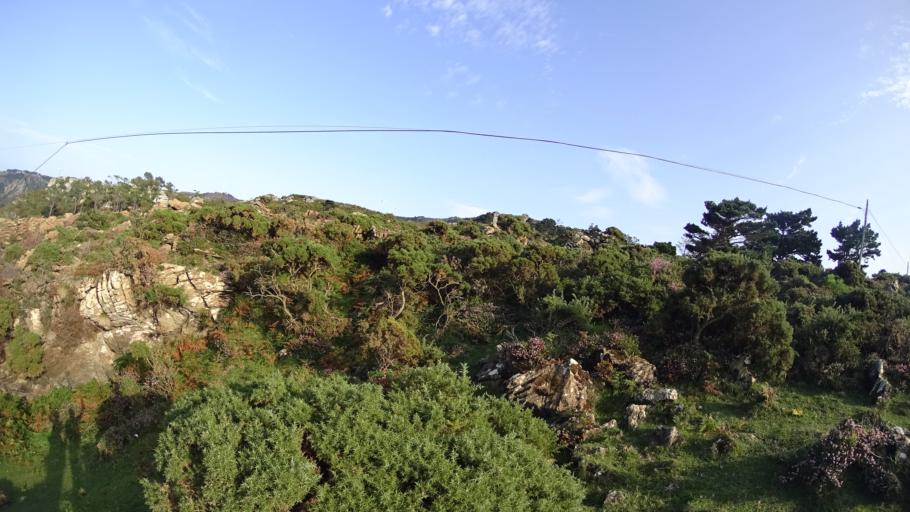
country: ES
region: Galicia
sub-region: Provincia da Coruna
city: Cedeira
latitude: 43.7026
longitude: -7.9904
